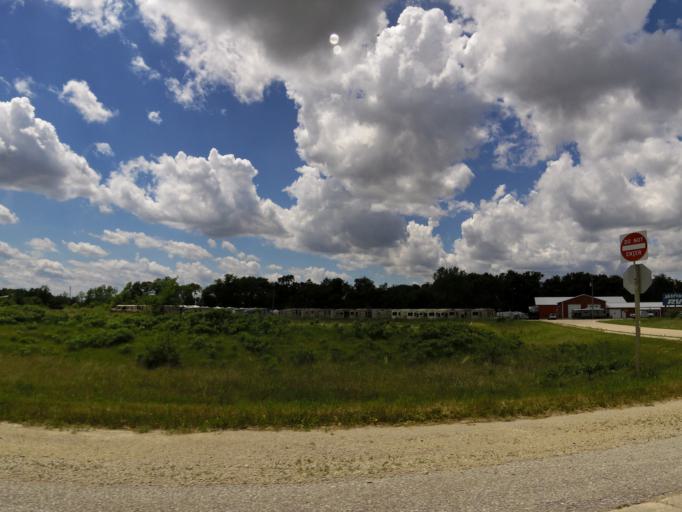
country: US
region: Iowa
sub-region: Fayette County
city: Oelwein
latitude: 42.5939
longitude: -91.9015
